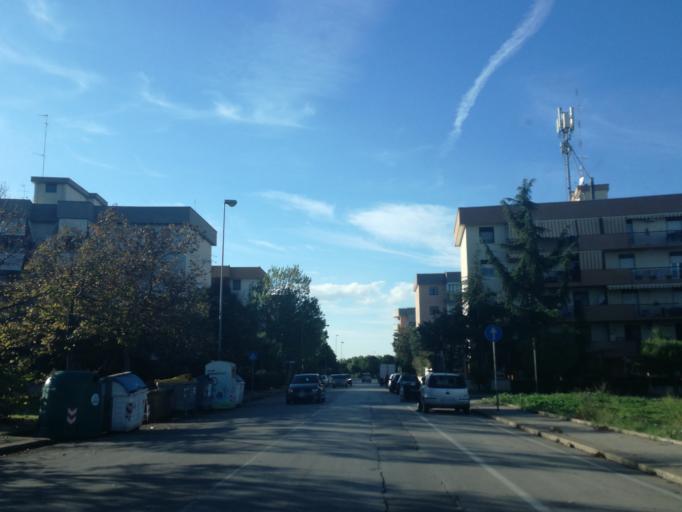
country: IT
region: Apulia
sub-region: Provincia di Bari
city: San Paolo
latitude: 41.1271
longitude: 16.7830
